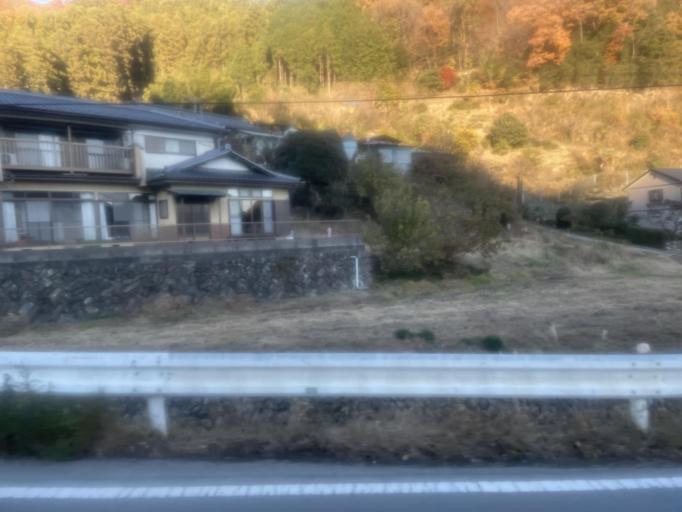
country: JP
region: Saitama
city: Yorii
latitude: 36.0798
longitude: 139.1761
